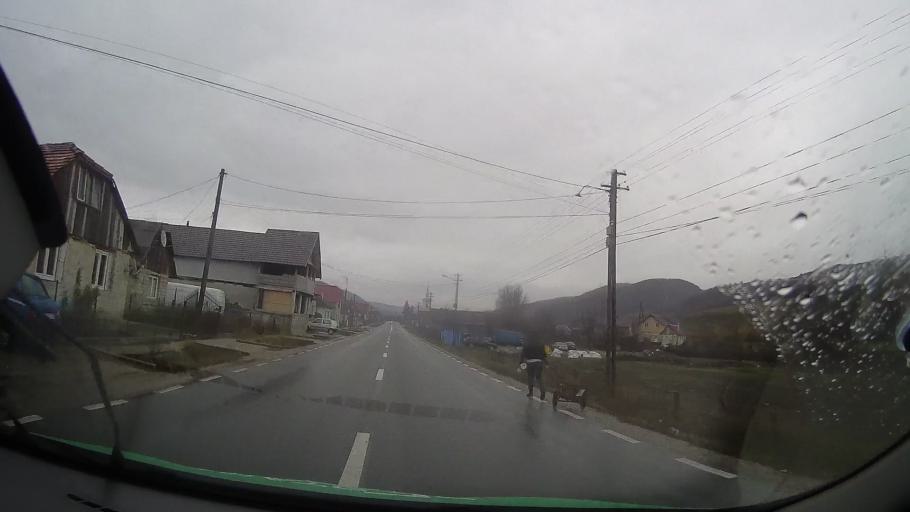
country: RO
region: Bistrita-Nasaud
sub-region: Comuna Galatii Bistritei
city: Galatii Bistritei
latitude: 46.9488
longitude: 24.4532
